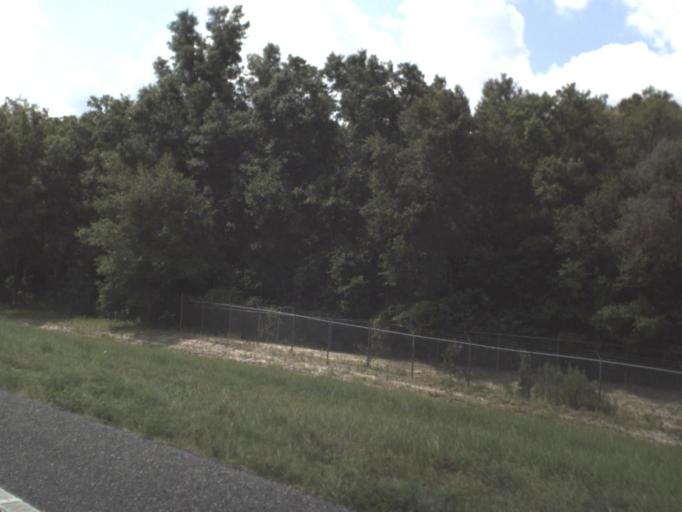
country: US
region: Florida
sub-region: Hernando County
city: Ridge Manor
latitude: 28.5085
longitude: -82.2010
